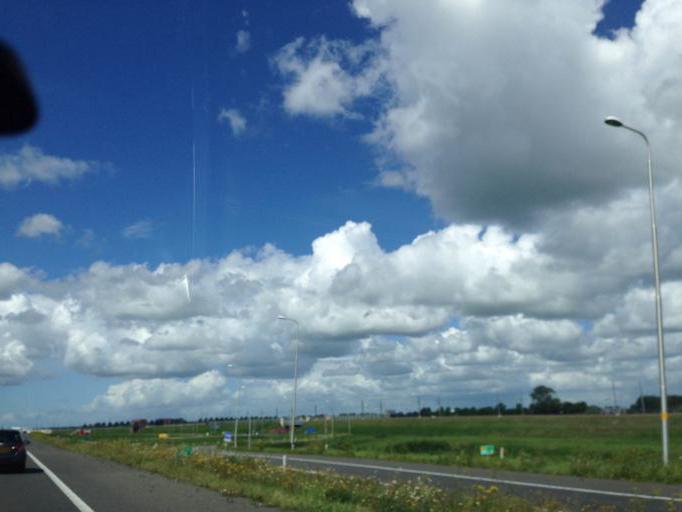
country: NL
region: Overijssel
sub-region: Gemeente Kampen
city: Kampen
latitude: 52.5275
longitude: 5.9187
